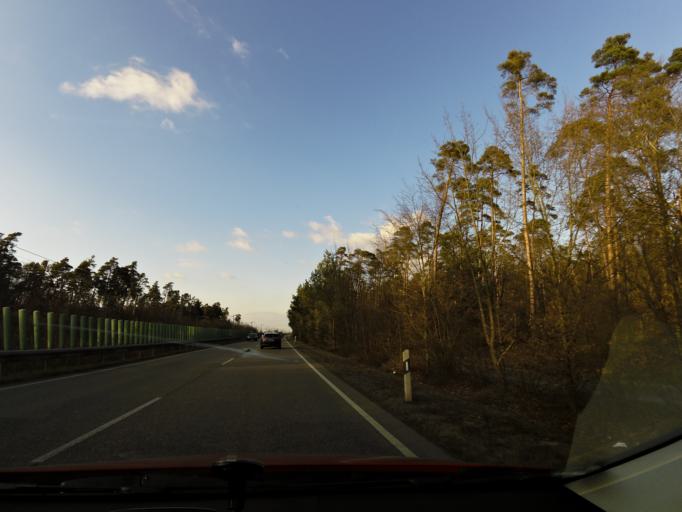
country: DE
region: Baden-Wuerttemberg
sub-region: Karlsruhe Region
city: Waghausel
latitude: 49.2354
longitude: 8.4961
